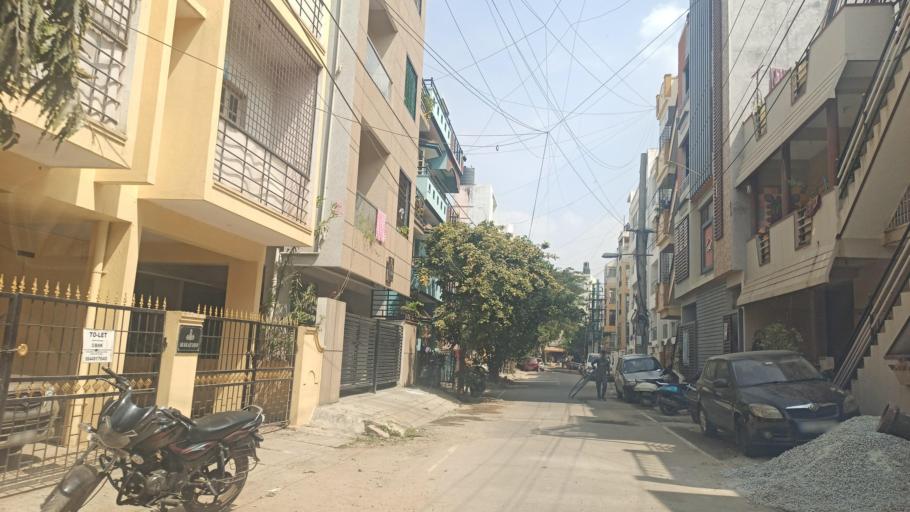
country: IN
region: Karnataka
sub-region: Bangalore Urban
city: Bangalore
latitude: 13.0356
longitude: 77.6002
